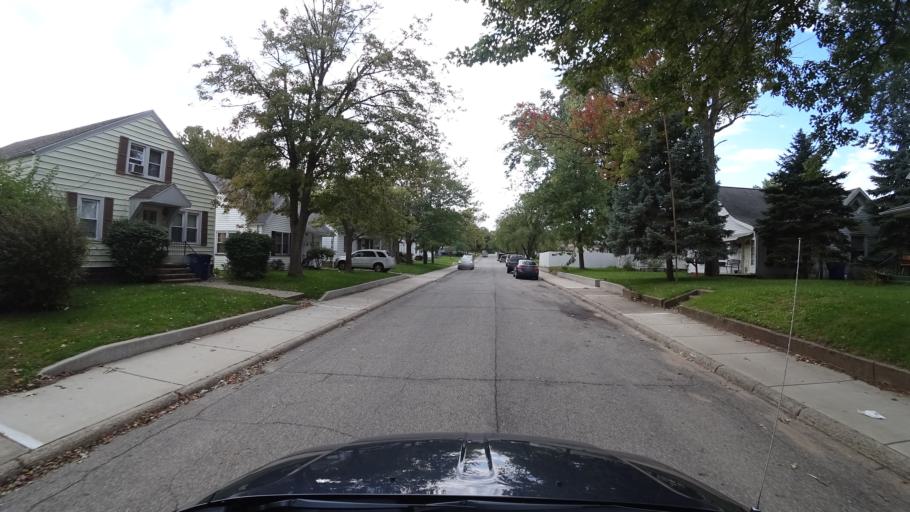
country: US
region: Indiana
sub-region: LaPorte County
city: Michigan City
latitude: 41.7089
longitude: -86.8773
